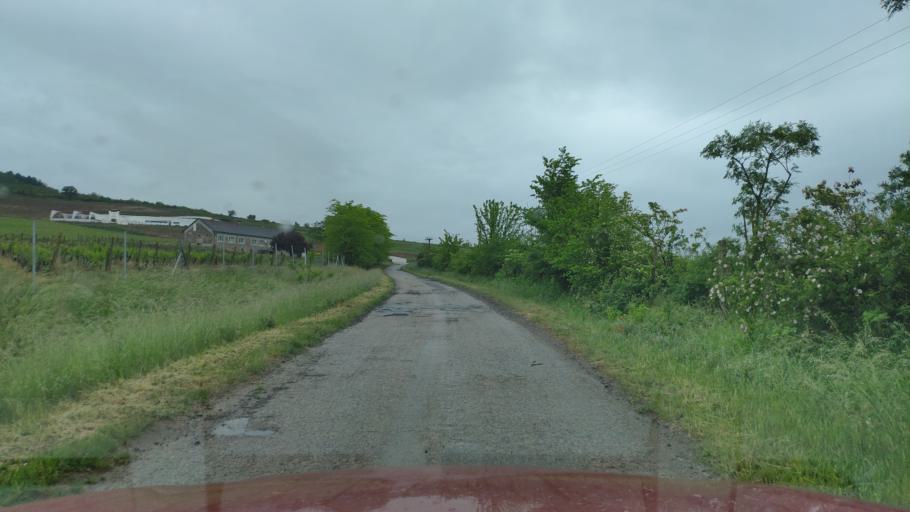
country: HU
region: Borsod-Abauj-Zemplen
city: Satoraljaujhely
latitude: 48.4189
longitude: 21.7050
